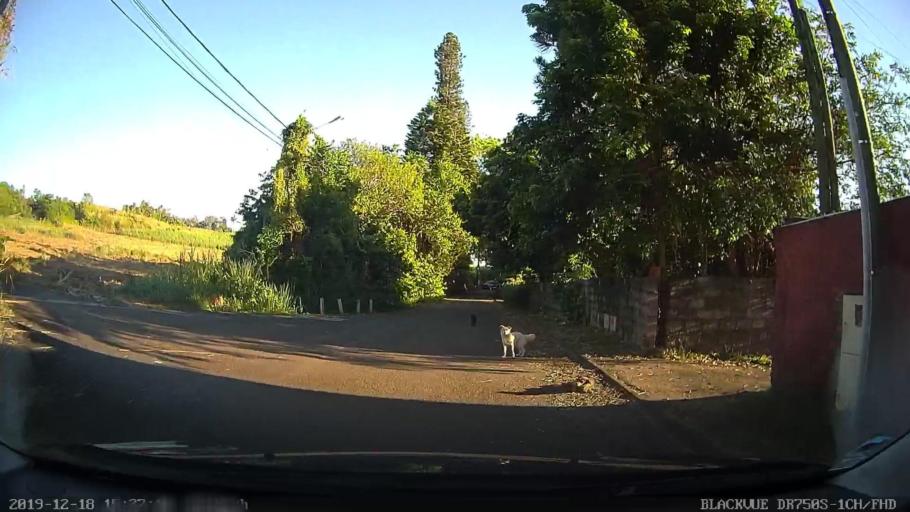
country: RE
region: Reunion
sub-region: Reunion
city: Bras-Panon
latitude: -21.0003
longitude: 55.6537
